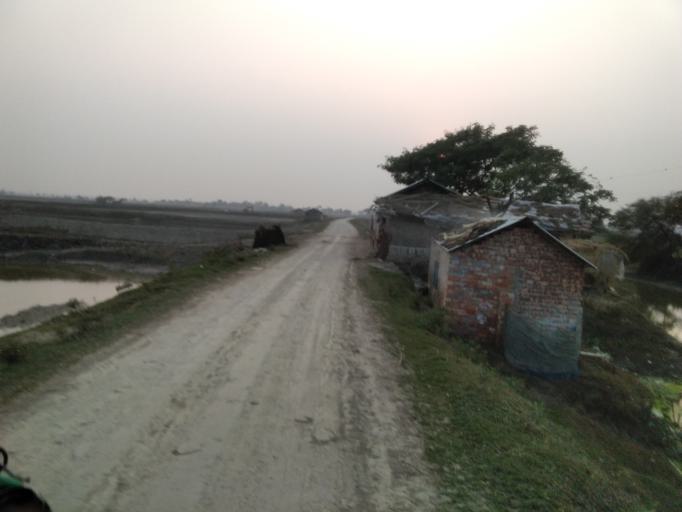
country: BD
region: Khulna
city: Satkhira
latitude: 22.6528
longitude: 89.0199
